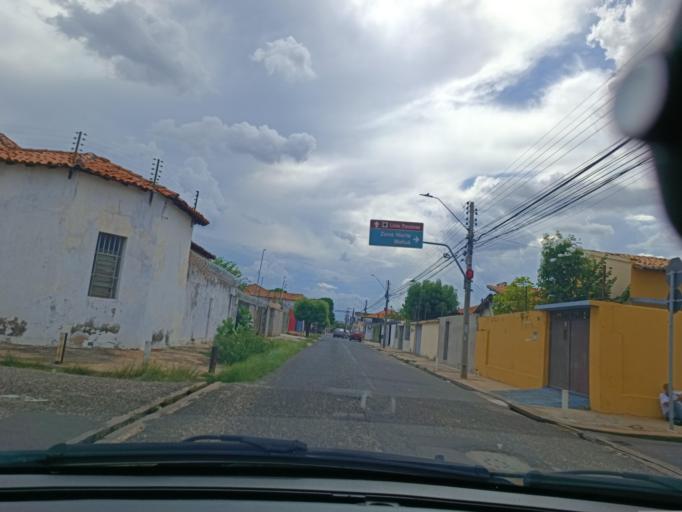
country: BR
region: Piaui
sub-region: Teresina
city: Teresina
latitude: -5.0837
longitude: -42.8114
